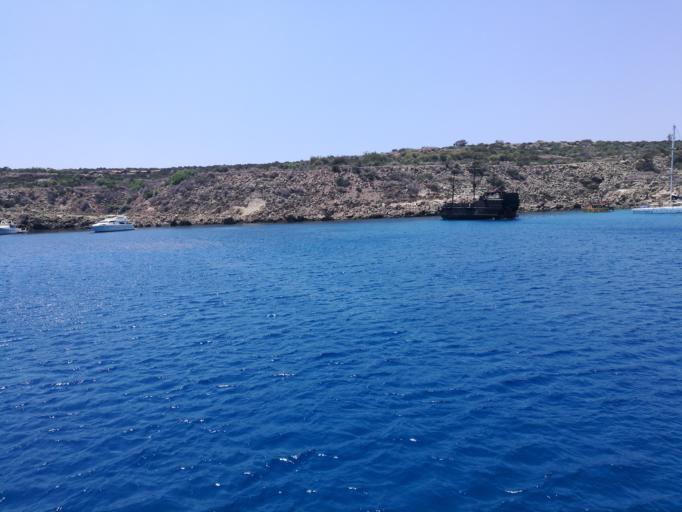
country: CY
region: Ammochostos
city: Protaras
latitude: 34.9785
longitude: 34.0746
